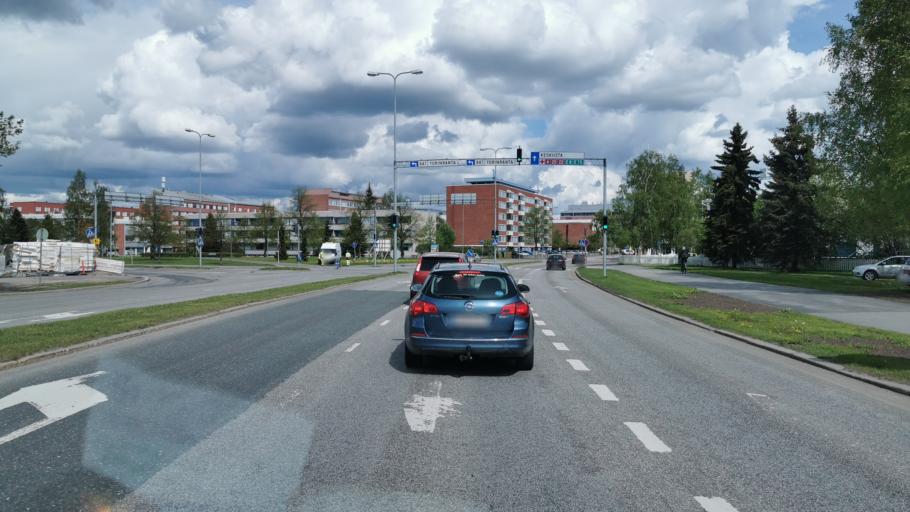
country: FI
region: Northern Ostrobothnia
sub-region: Oulu
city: Oulu
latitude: 65.0033
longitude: 25.4637
